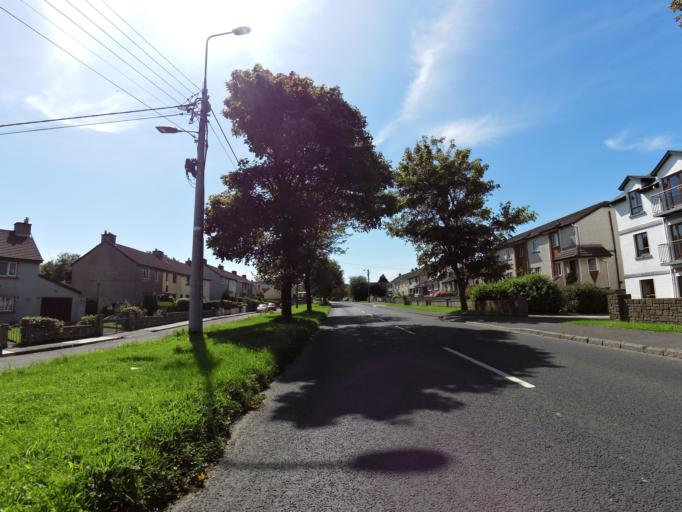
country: IE
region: Connaught
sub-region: County Galway
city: Gaillimh
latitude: 53.2748
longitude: -9.0746
